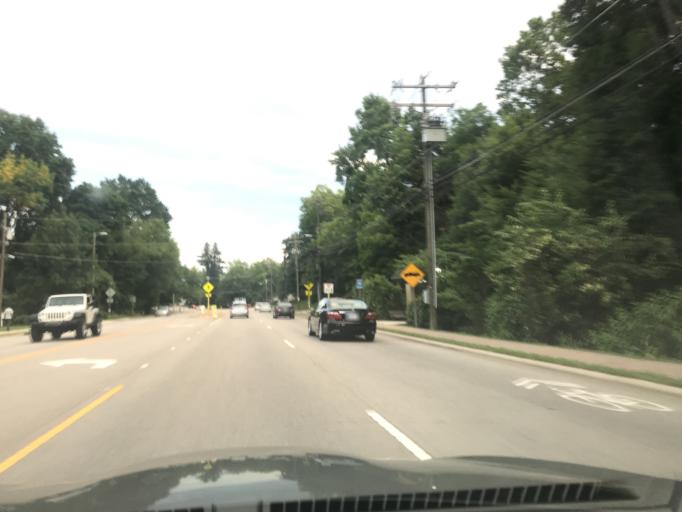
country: US
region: North Carolina
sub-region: Orange County
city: Chapel Hill
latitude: 35.9171
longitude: -79.0567
